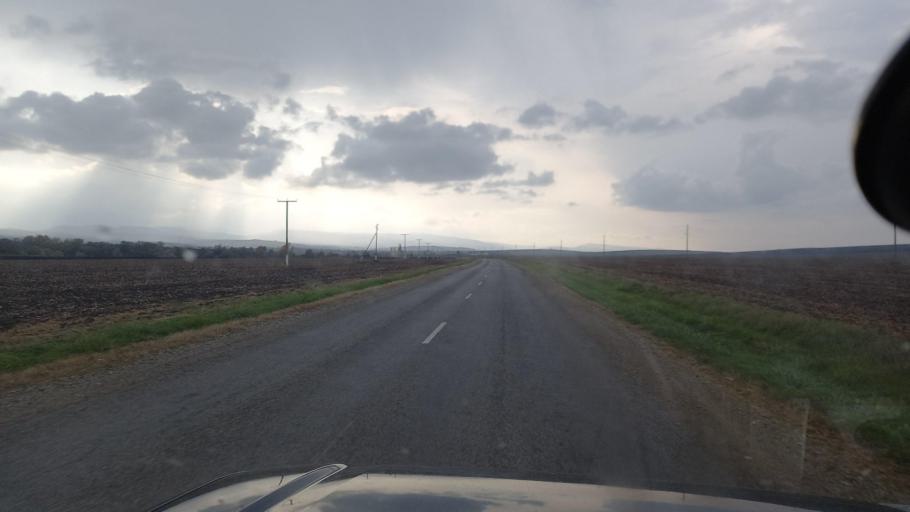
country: RU
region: Krasnodarskiy
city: Gubskaya
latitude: 44.3484
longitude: 40.6905
